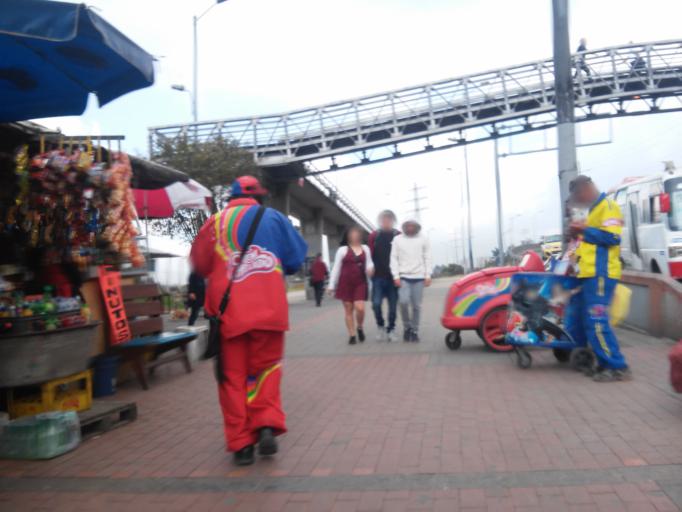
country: CO
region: Cundinamarca
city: Soacha
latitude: 4.5966
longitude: -74.1722
